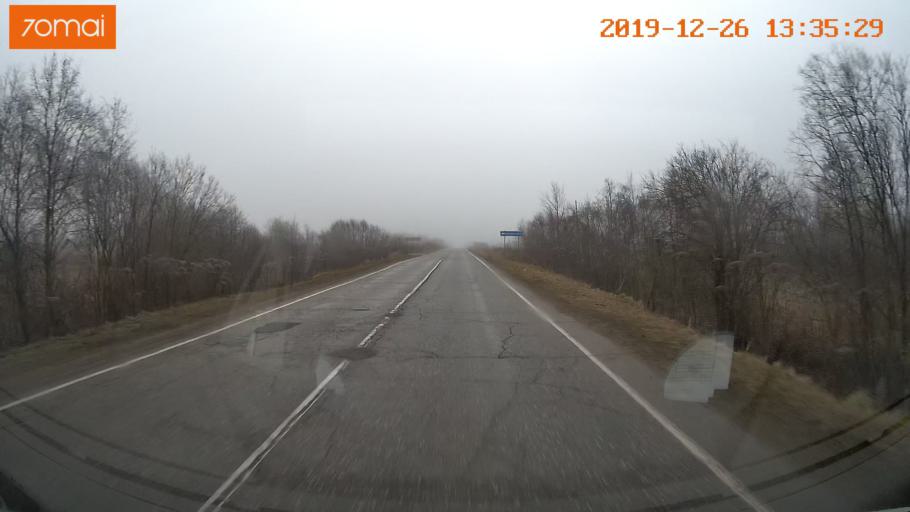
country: RU
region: Vologda
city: Sheksna
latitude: 58.7927
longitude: 38.3412
